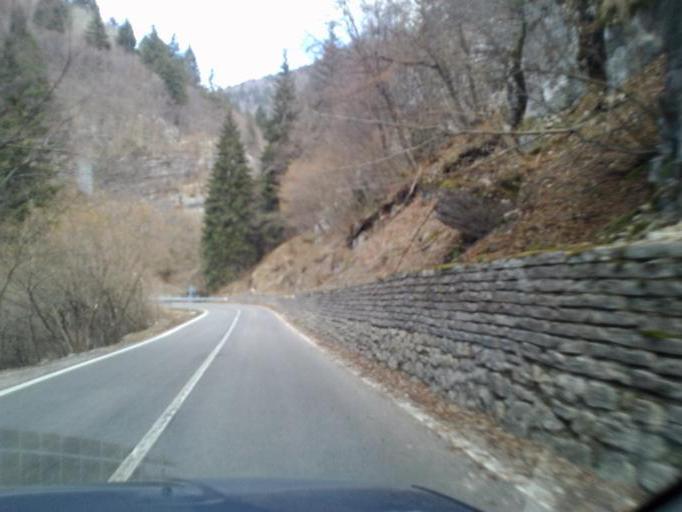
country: IT
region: Veneto
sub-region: Provincia di Verona
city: Erbezzo
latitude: 45.6574
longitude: 10.9828
